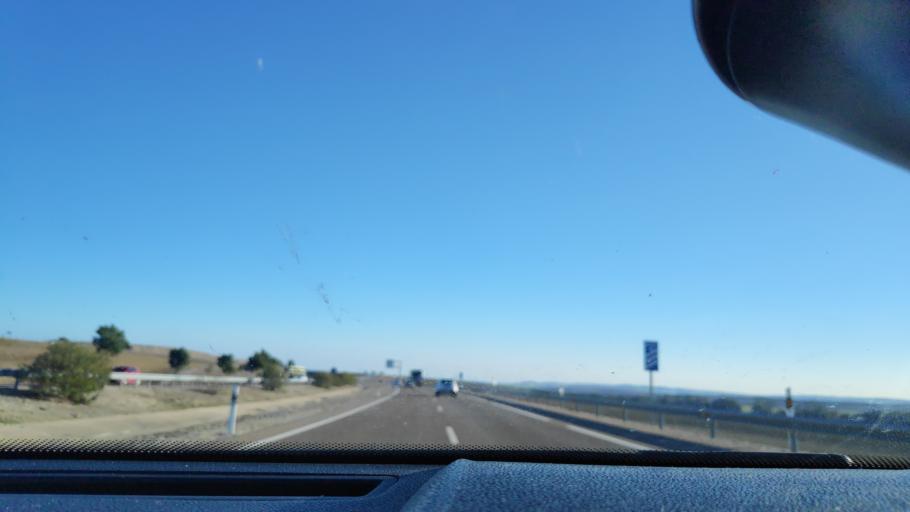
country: ES
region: Andalusia
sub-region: Provincia de Sevilla
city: Guillena
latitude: 37.5395
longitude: -6.0987
